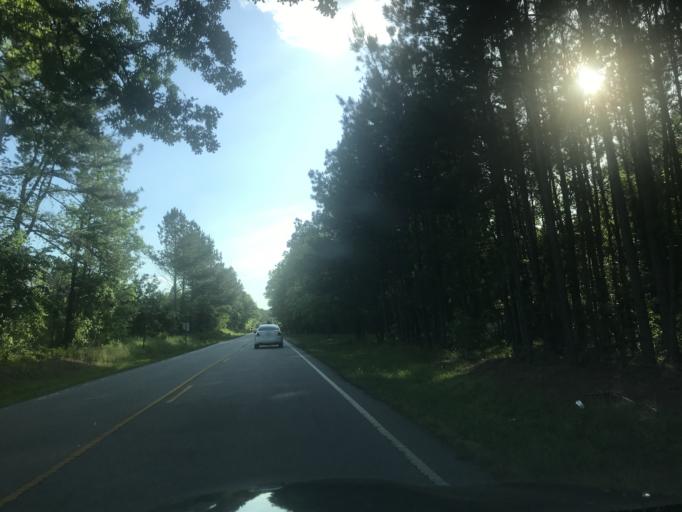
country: US
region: North Carolina
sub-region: Wake County
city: Knightdale
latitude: 35.7494
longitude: -78.4332
